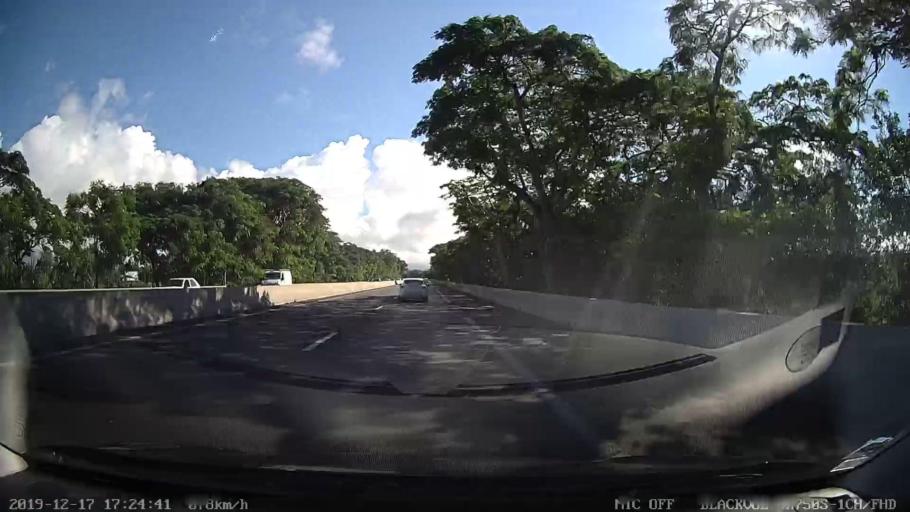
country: RE
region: Reunion
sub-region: Reunion
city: Le Tampon
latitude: -21.3008
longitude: 55.5040
